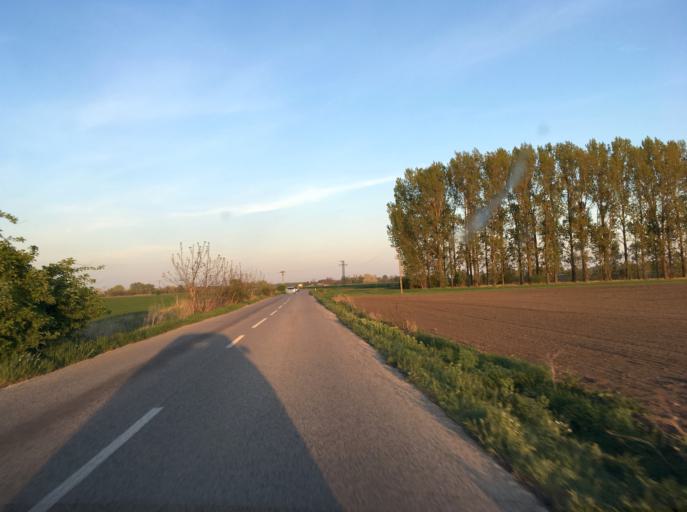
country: SK
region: Nitriansky
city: Kolarovo
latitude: 47.9016
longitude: 17.8844
